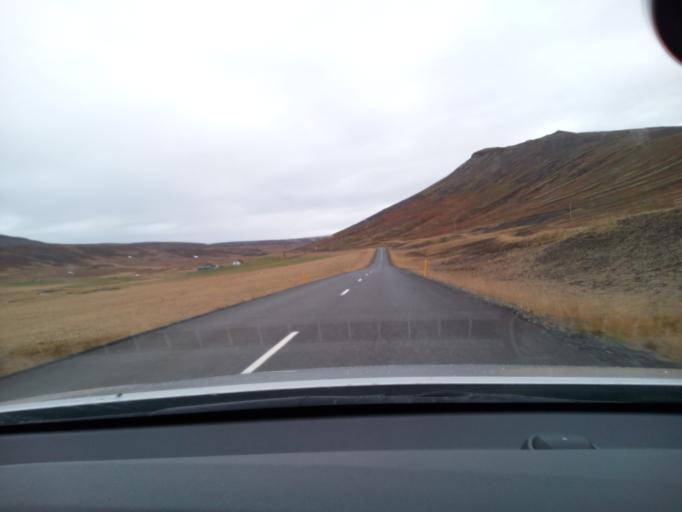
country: IS
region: Northeast
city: Laugar
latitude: 65.8027
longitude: -17.2614
